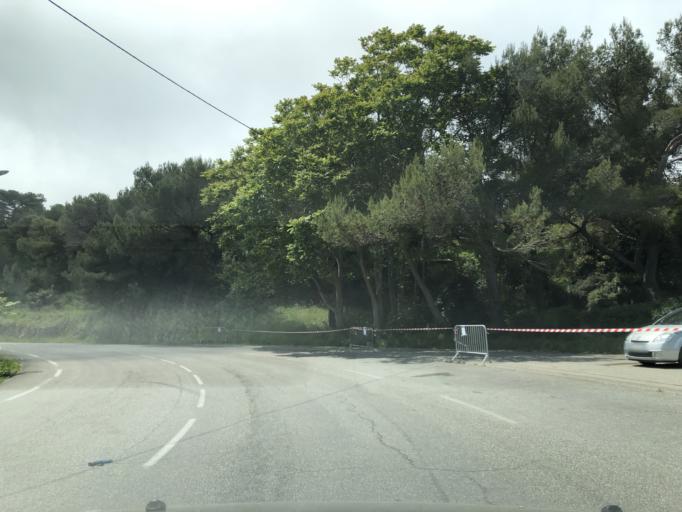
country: FR
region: Provence-Alpes-Cote d'Azur
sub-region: Departement des Alpes-Maritimes
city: Beaulieu-sur-Mer
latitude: 43.7311
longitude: 7.3416
